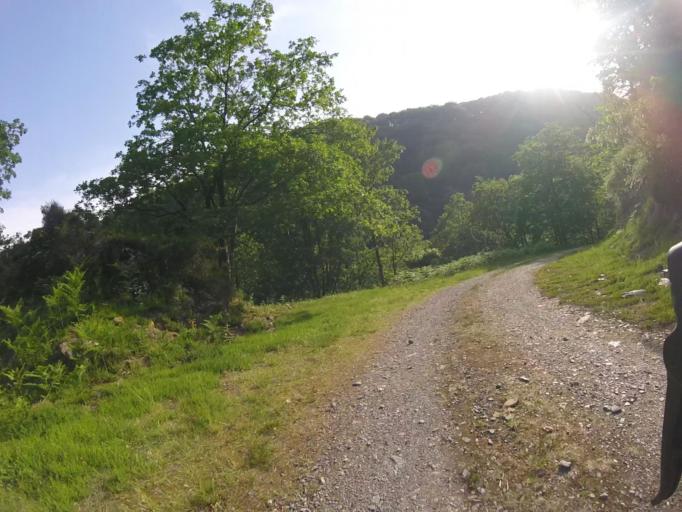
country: ES
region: Navarre
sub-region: Provincia de Navarra
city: Arano
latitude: 43.2356
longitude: -1.8710
